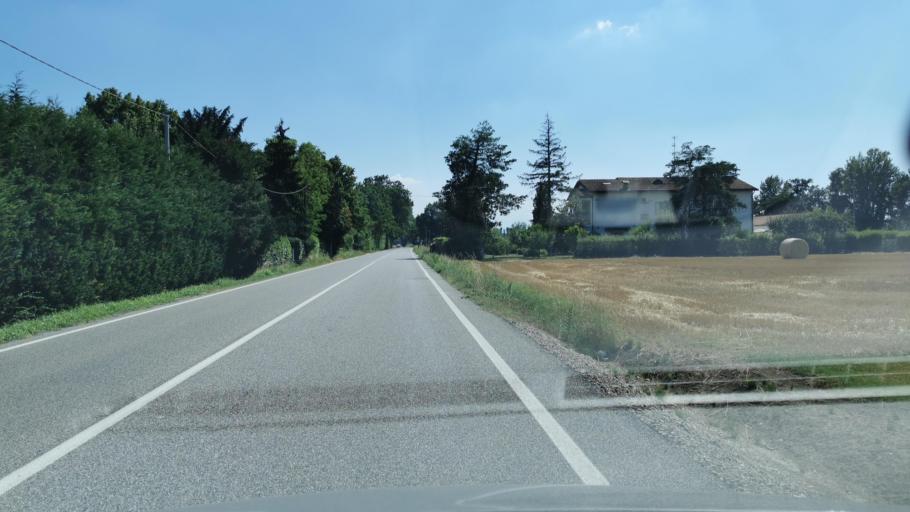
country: IT
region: Emilia-Romagna
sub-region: Provincia di Modena
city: Sam Marino
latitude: 44.7921
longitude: 10.9111
